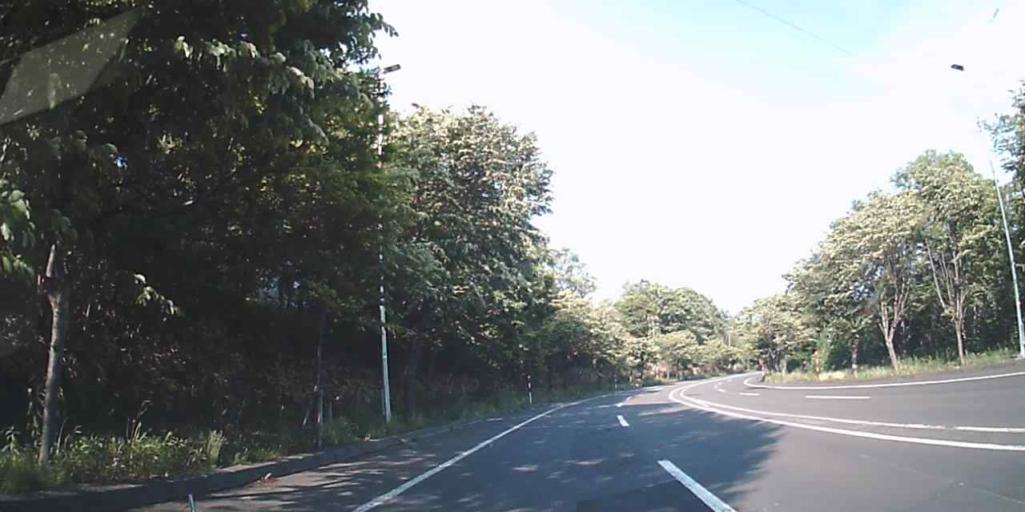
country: JP
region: Hokkaido
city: Shiraoi
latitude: 42.4655
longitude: 141.1742
